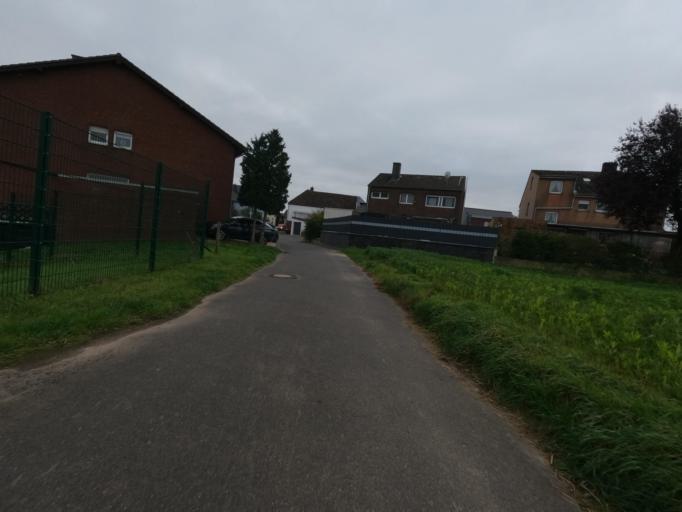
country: DE
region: North Rhine-Westphalia
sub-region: Regierungsbezirk Koln
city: Linnich
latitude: 50.9597
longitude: 6.2843
